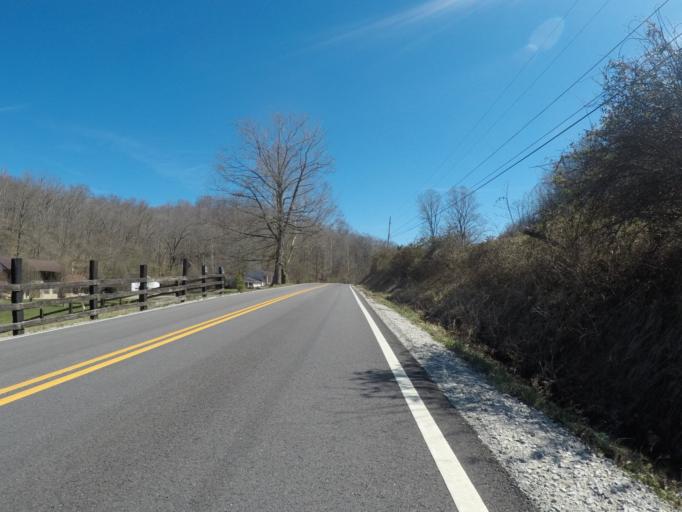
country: US
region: Ohio
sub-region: Lawrence County
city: South Point
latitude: 38.4655
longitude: -82.5673
